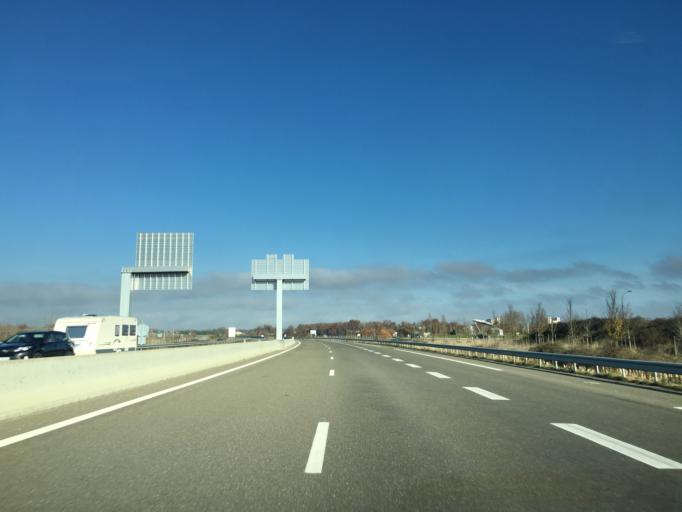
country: FR
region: Midi-Pyrenees
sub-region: Departement du Gers
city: Barcelonne-du-Gers
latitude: 43.7223
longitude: -0.2720
